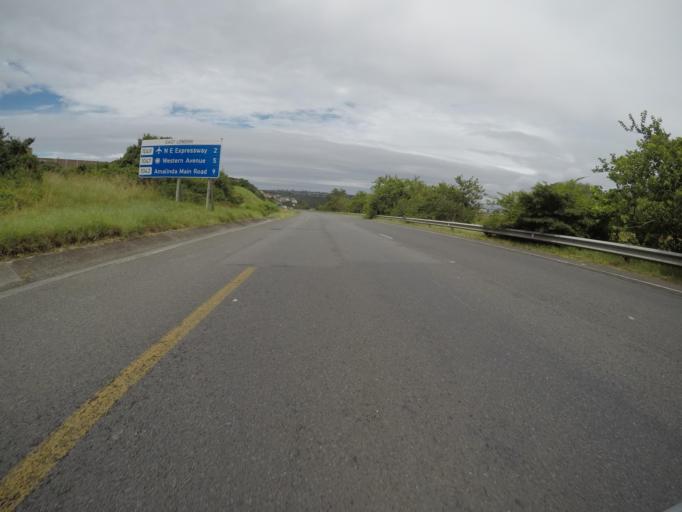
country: ZA
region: Eastern Cape
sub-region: Buffalo City Metropolitan Municipality
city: East London
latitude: -32.9533
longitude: 27.9309
